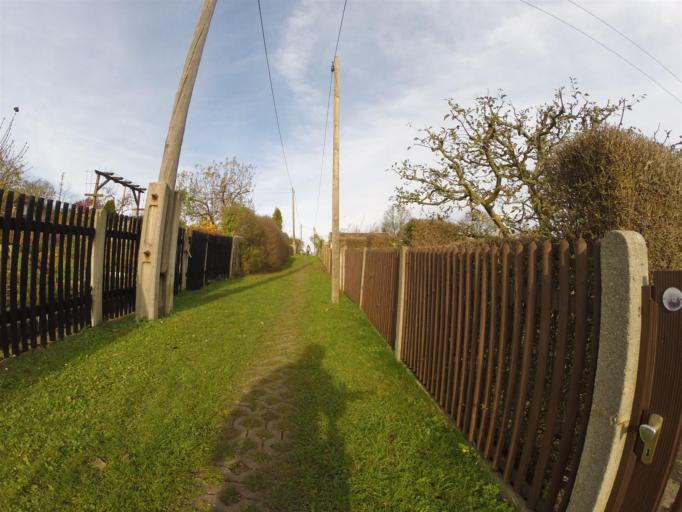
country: DE
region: Thuringia
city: Jena
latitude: 50.9240
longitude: 11.5630
